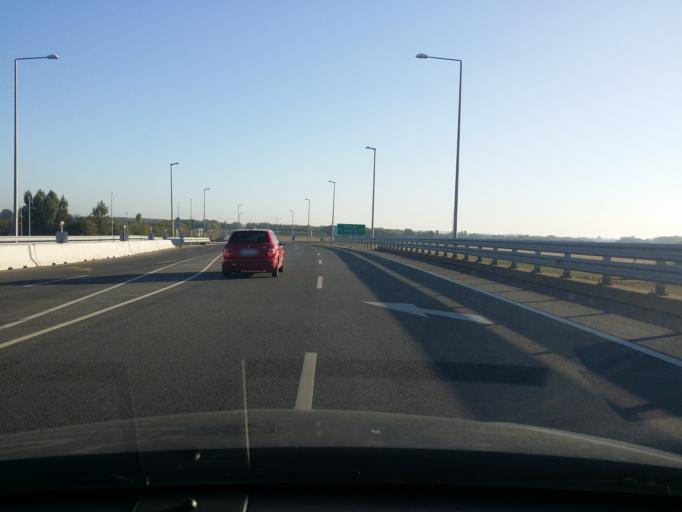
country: HU
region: Bacs-Kiskun
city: Kecskemet
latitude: 46.9404
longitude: 19.6587
